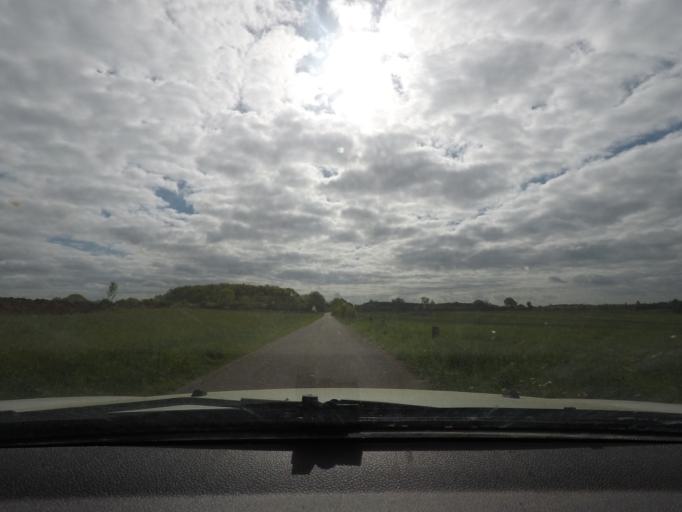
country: BE
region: Wallonia
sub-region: Province du Luxembourg
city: Habay-la-Vieille
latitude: 49.7149
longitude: 5.5944
